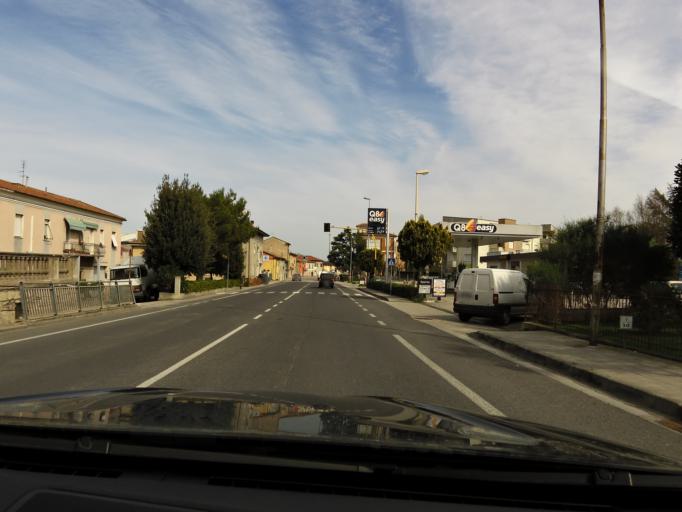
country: IT
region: The Marches
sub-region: Provincia di Ancona
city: Camerano
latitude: 43.4971
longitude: 13.5425
